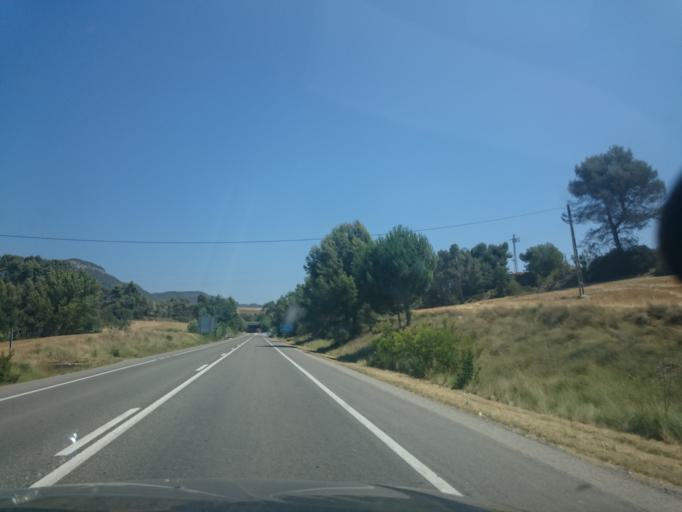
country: ES
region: Catalonia
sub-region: Provincia de Barcelona
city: Odena
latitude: 41.5835
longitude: 1.6717
